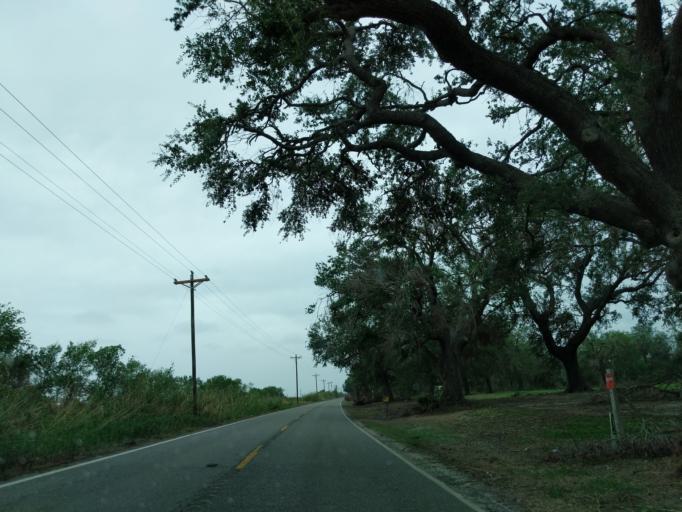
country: US
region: Louisiana
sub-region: Jefferson Davis Parish
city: Lake Arthur
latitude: 29.7528
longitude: -92.9119
